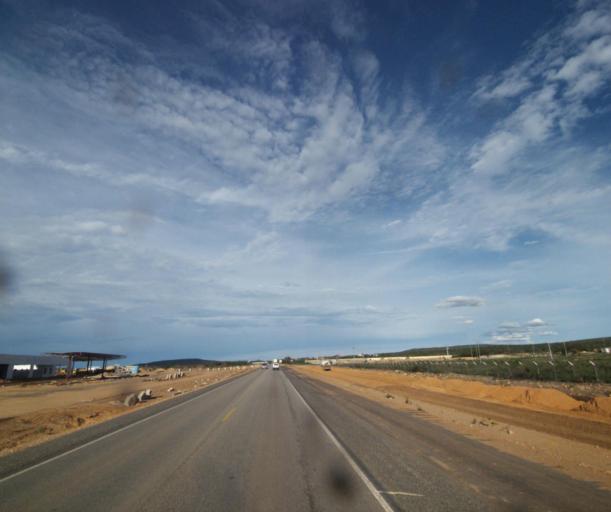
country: BR
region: Bahia
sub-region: Caetite
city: Caetite
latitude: -14.0733
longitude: -42.5420
